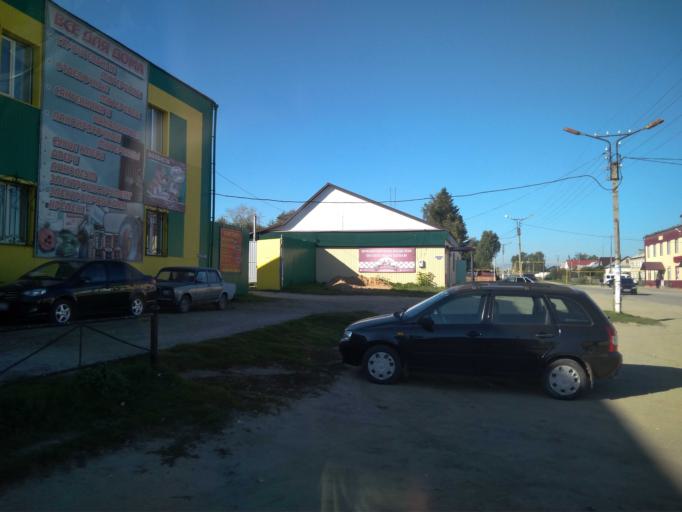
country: RU
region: Mordoviya
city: Chamzinka
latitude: 54.1747
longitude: 45.9689
